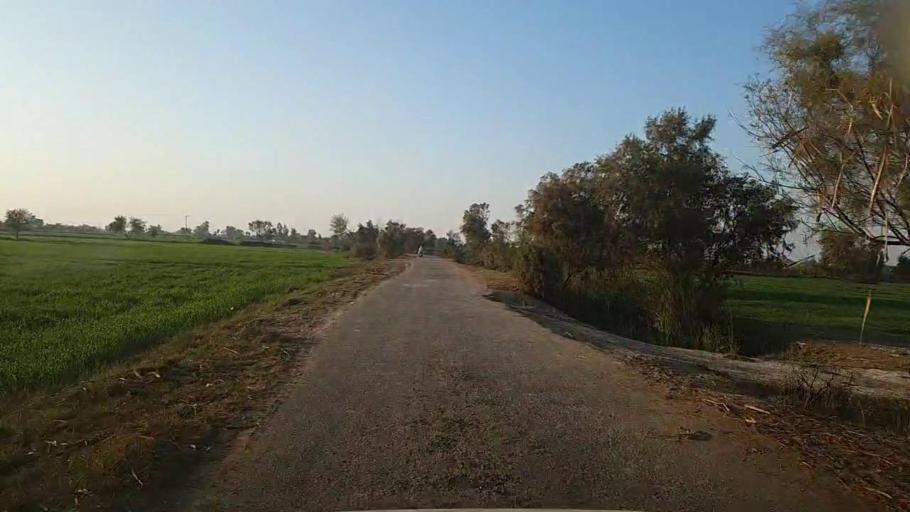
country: PK
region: Sindh
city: Mirpur Mathelo
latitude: 27.8759
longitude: 69.6514
